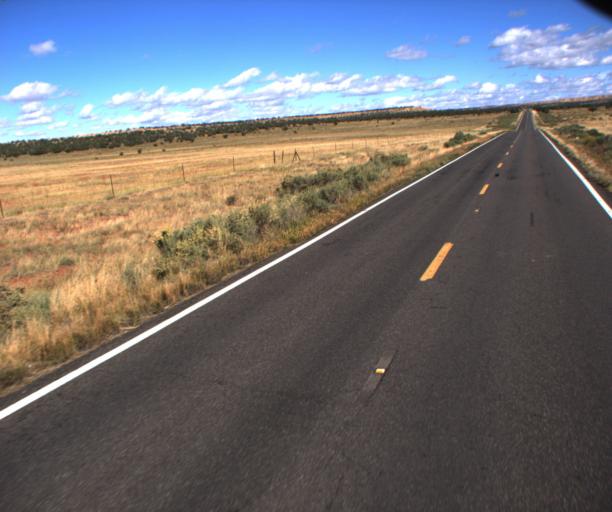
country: US
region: Arizona
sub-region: Apache County
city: Saint Johns
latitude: 34.7659
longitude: -109.2414
